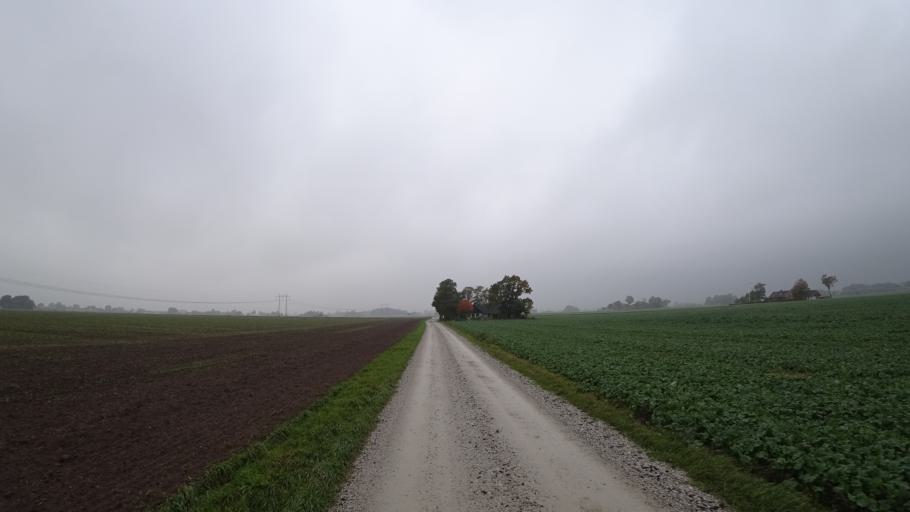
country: SE
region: Skane
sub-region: Kavlinge Kommun
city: Kaevlinge
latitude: 55.8115
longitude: 13.1669
